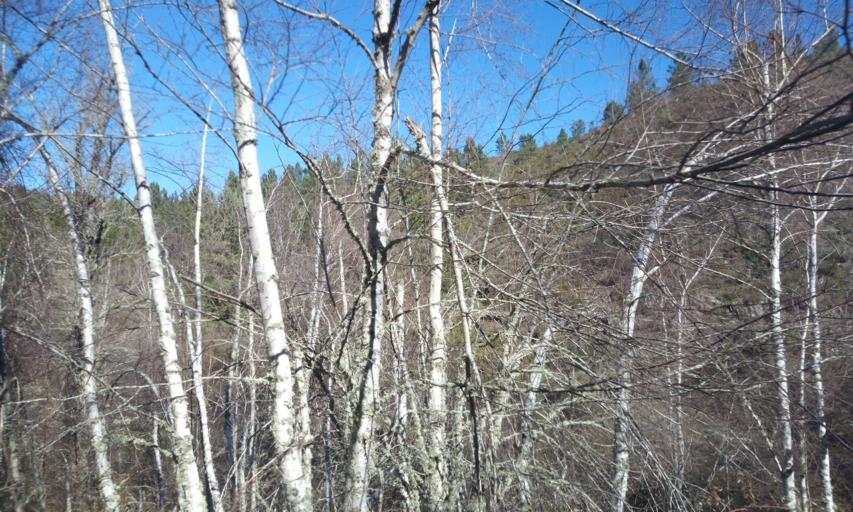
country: PT
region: Guarda
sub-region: Manteigas
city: Manteigas
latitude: 40.4409
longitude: -7.5052
